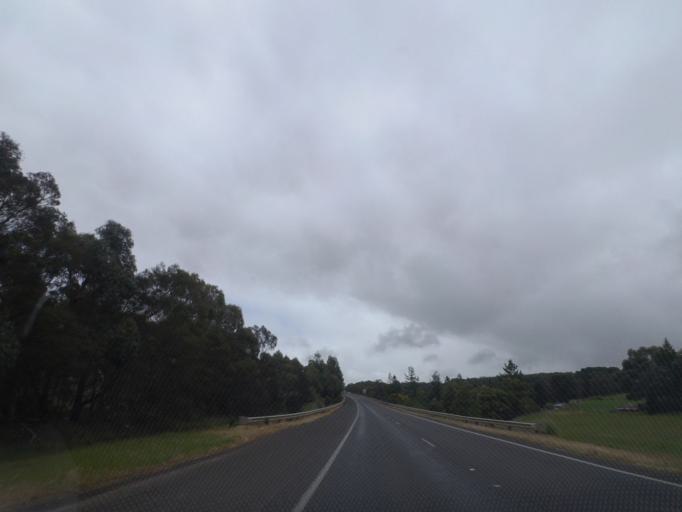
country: AU
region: Victoria
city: Brown Hill
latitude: -37.5436
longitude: 143.8900
